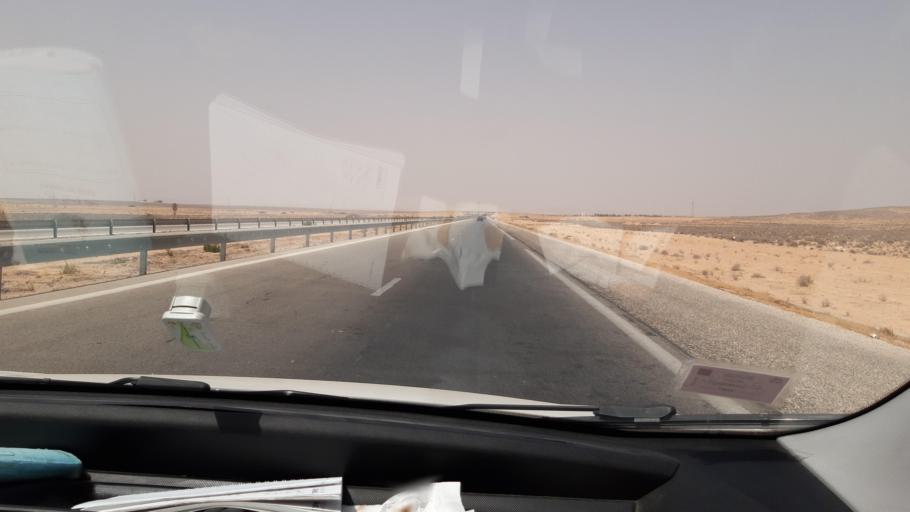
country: TN
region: Qabis
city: Gabes
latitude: 33.9028
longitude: 9.9783
